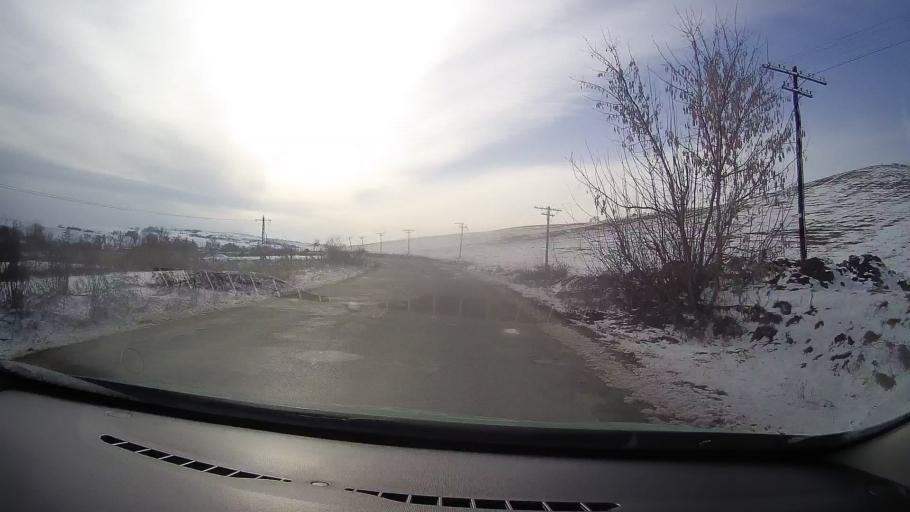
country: RO
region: Sibiu
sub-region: Oras Agnita
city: Ruja
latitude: 45.9944
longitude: 24.6657
